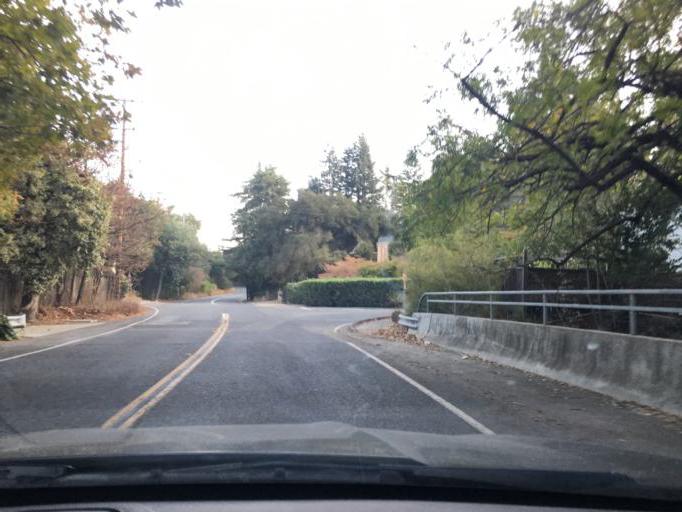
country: US
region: California
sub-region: Santa Clara County
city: Monte Sereno
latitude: 37.2429
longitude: -121.9985
